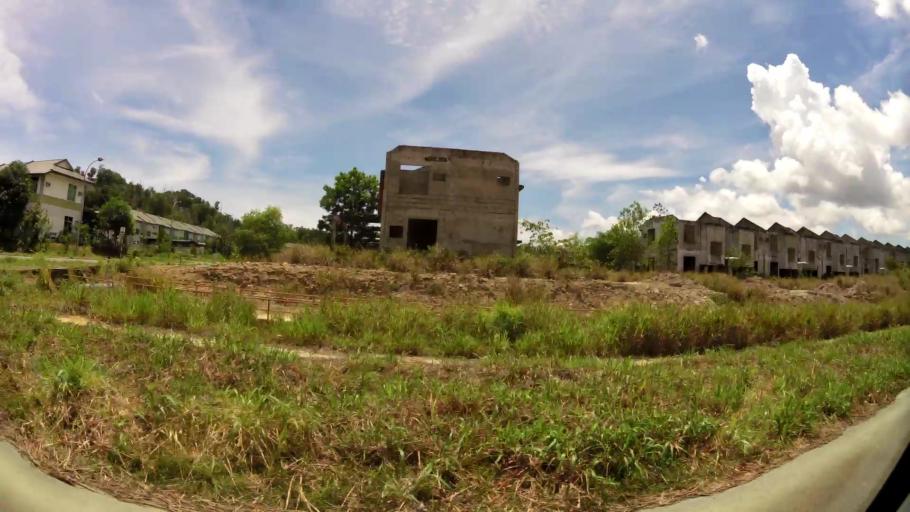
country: BN
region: Brunei and Muara
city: Bandar Seri Begawan
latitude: 4.9685
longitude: 114.9104
